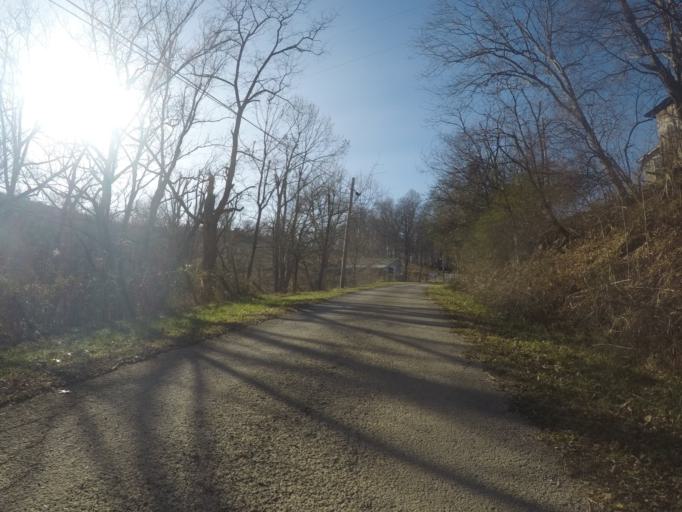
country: US
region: Ohio
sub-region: Lawrence County
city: Burlington
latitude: 38.3902
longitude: -82.4923
